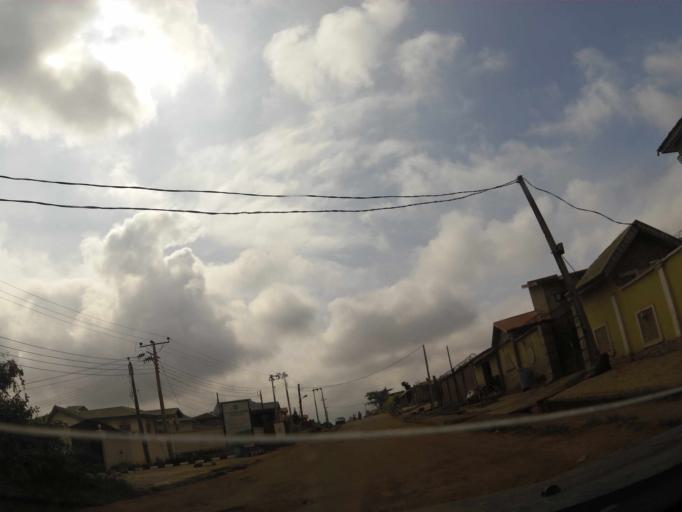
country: NG
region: Oyo
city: Ibadan
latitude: 7.4417
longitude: 3.9542
